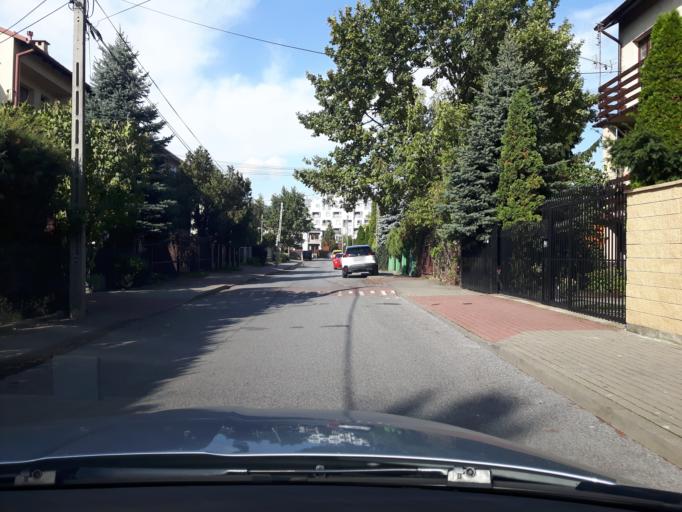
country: PL
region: Masovian Voivodeship
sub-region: Powiat wolominski
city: Zabki
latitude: 52.2852
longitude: 21.0801
